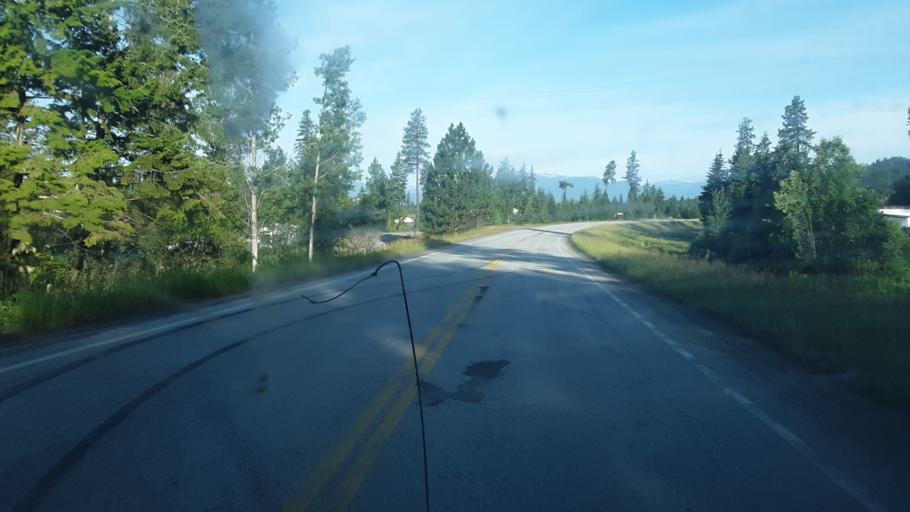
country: US
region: Idaho
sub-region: Boundary County
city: Bonners Ferry
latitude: 48.7219
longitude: -116.1652
